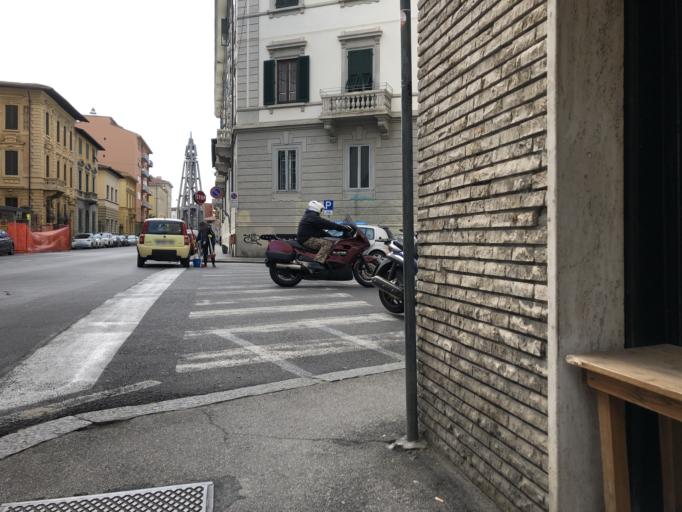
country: IT
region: Tuscany
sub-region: Province of Florence
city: Florence
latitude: 43.7758
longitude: 11.2757
